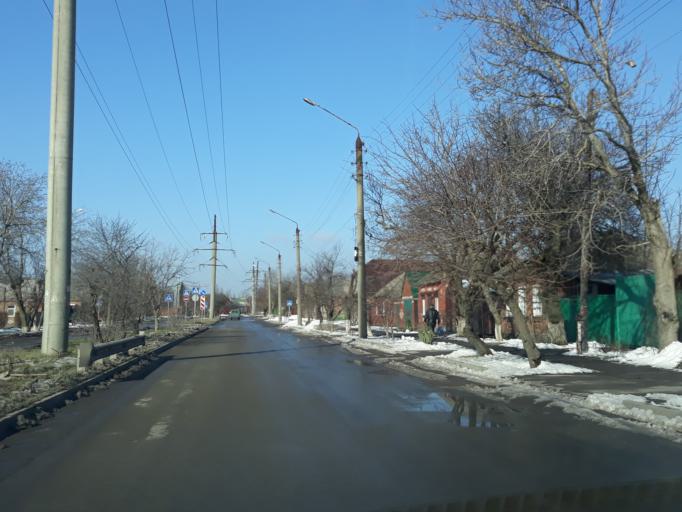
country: RU
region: Rostov
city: Taganrog
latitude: 47.2199
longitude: 38.8783
